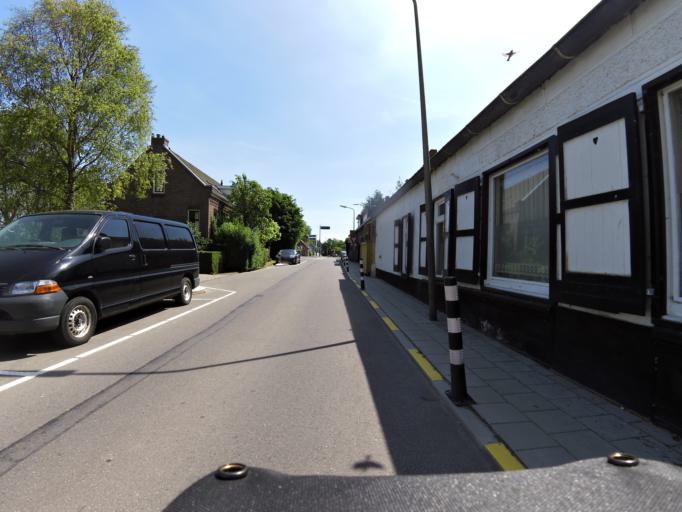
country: NL
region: South Holland
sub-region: Gemeente Spijkenisse
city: Spijkenisse
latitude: 51.7918
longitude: 4.3129
